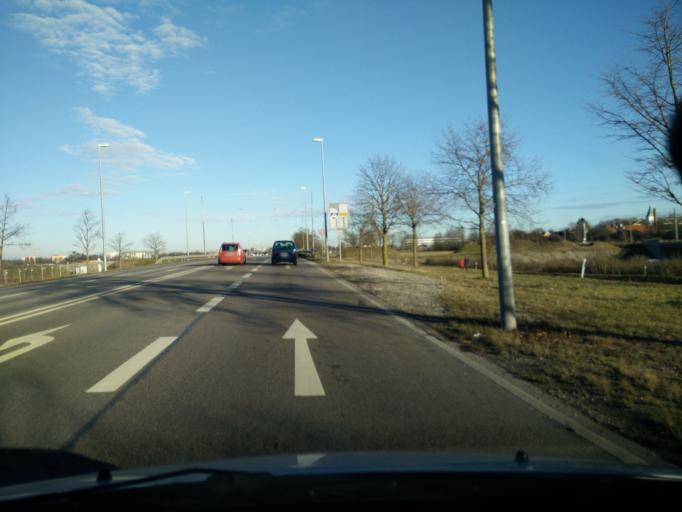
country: DE
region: Bavaria
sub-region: Upper Bavaria
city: Germering
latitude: 48.1377
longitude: 11.3951
